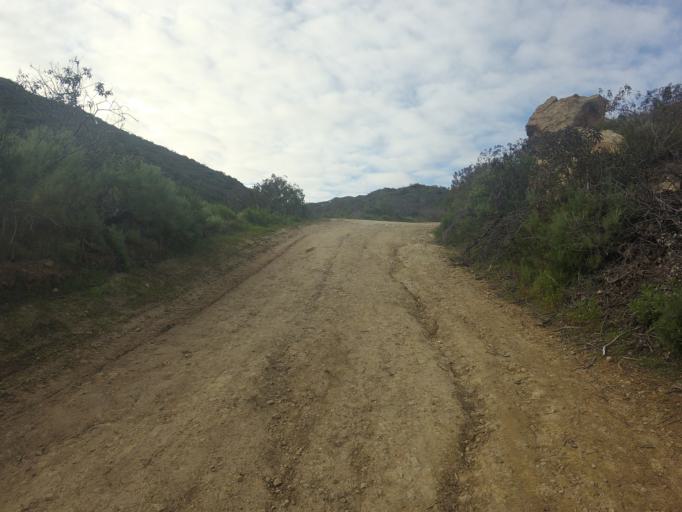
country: US
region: California
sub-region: Orange County
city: Aliso Viejo
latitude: 33.5827
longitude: -117.7650
